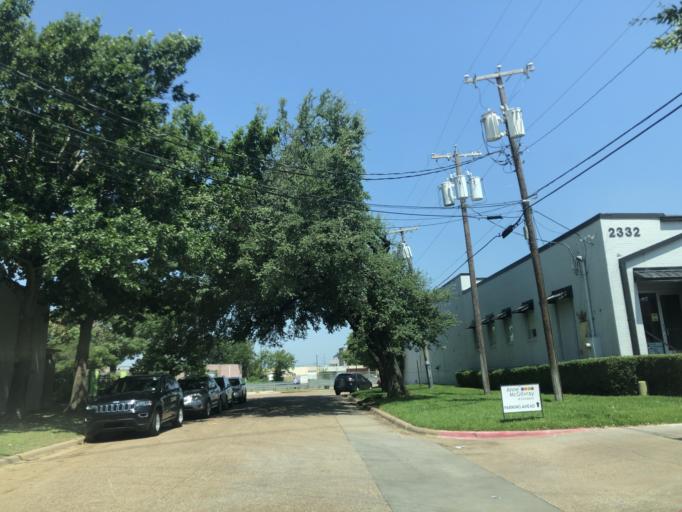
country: US
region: Texas
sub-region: Dallas County
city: Dallas
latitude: 32.8015
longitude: -96.8356
